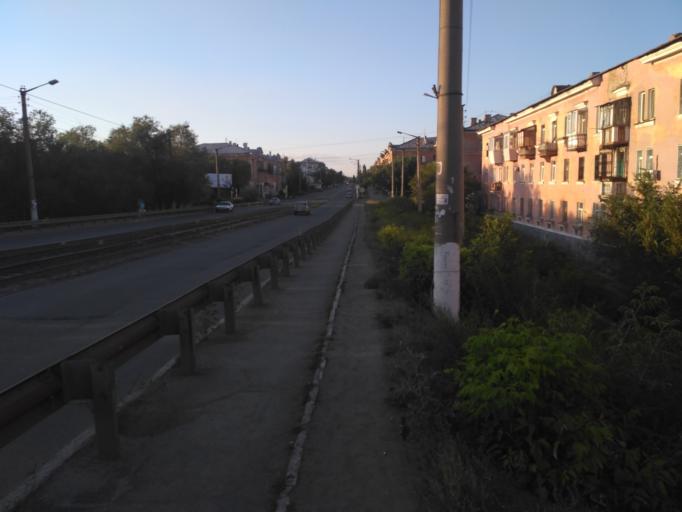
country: RU
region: Orenburg
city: Novotroitsk
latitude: 51.2021
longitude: 58.2991
